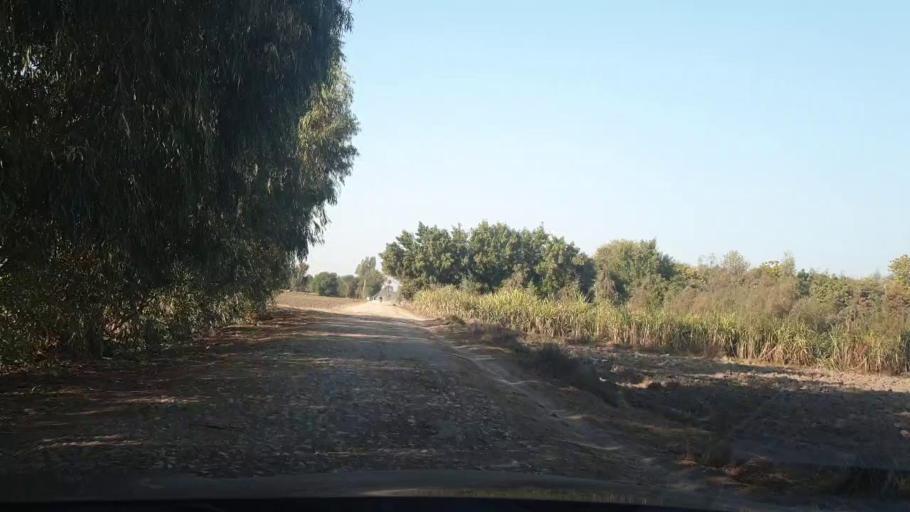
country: PK
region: Sindh
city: Ubauro
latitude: 28.1481
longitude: 69.6097
